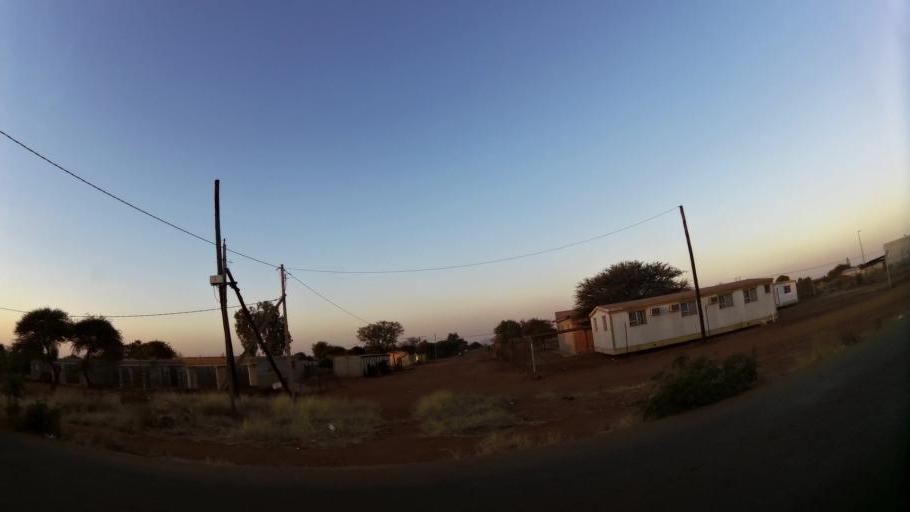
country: ZA
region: North-West
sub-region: Bojanala Platinum District Municipality
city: Rustenburg
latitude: -25.6152
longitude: 27.1931
